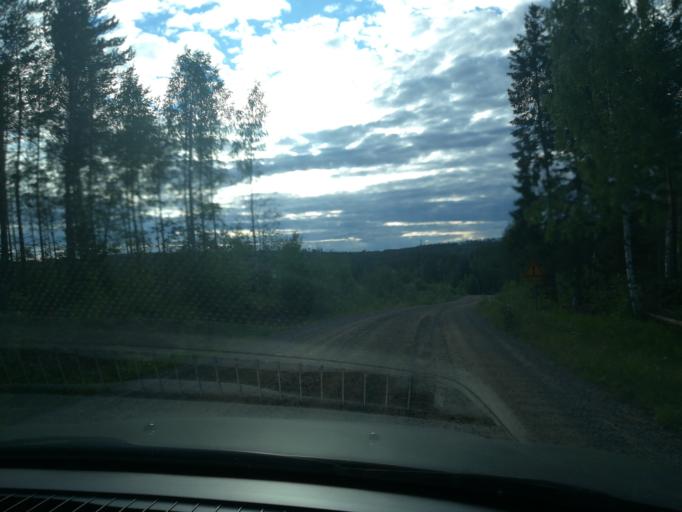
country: FI
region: Southern Savonia
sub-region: Mikkeli
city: Puumala
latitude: 61.5900
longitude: 28.1598
